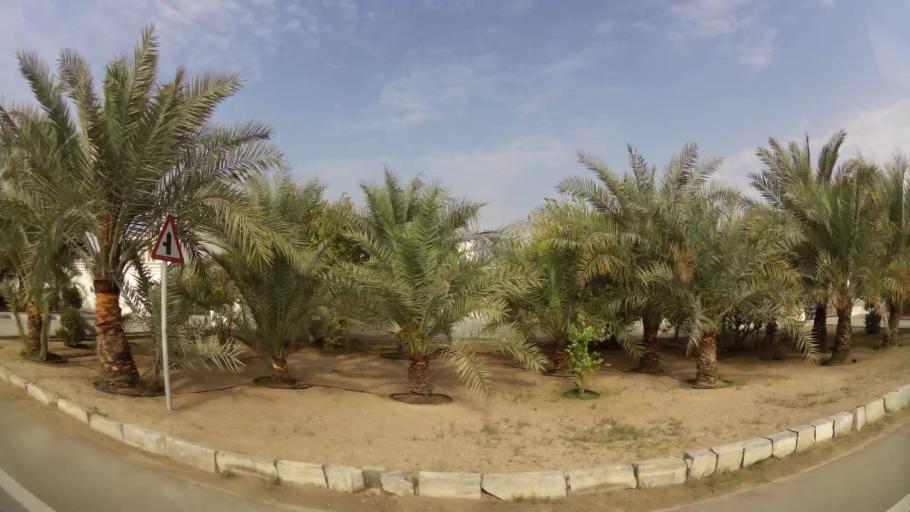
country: AE
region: Abu Dhabi
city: Abu Dhabi
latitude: 24.6602
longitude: 54.7594
